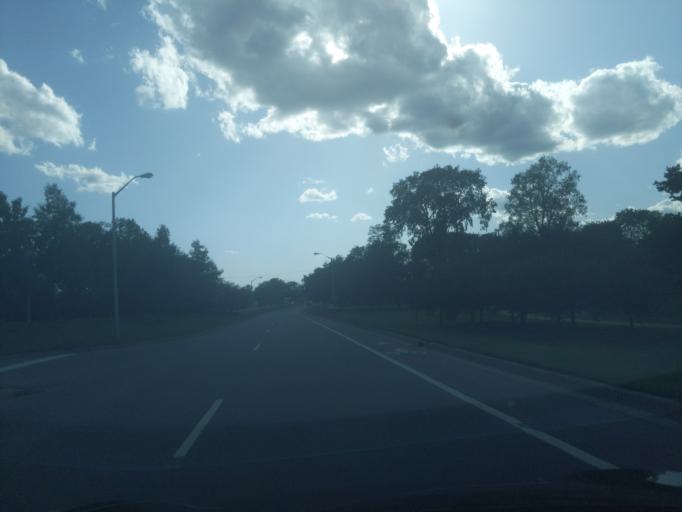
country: US
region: Michigan
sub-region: Ingham County
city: East Lansing
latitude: 42.7201
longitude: -84.4912
